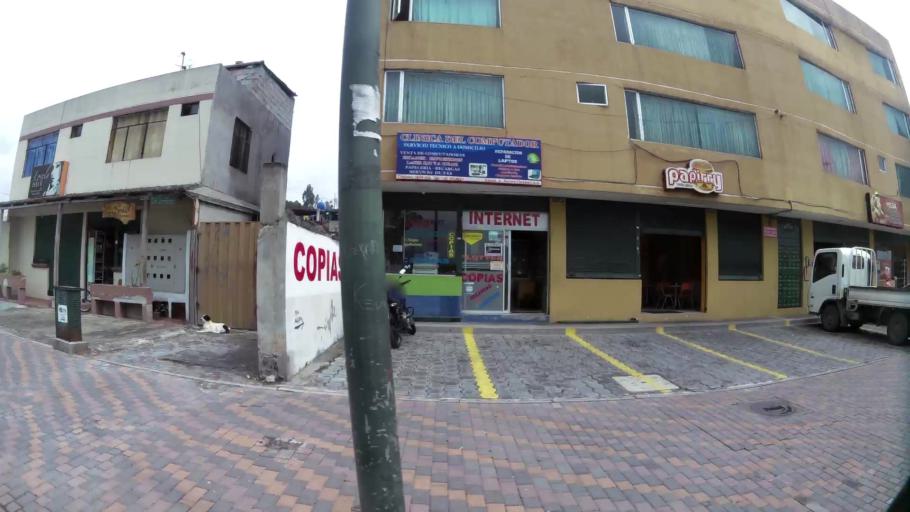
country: EC
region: Pichincha
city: Sangolqui
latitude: -0.3105
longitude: -78.4721
